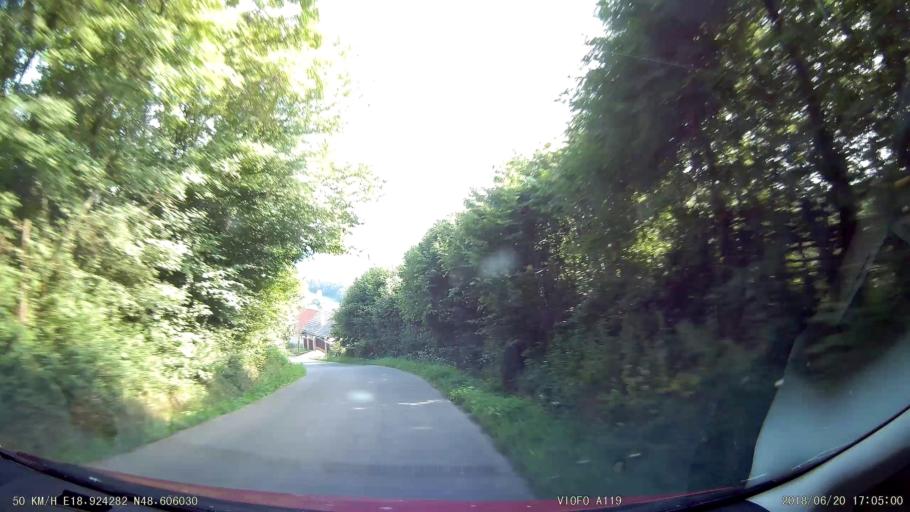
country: SK
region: Banskobystricky
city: Ziar nad Hronom
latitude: 48.6060
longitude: 18.9239
